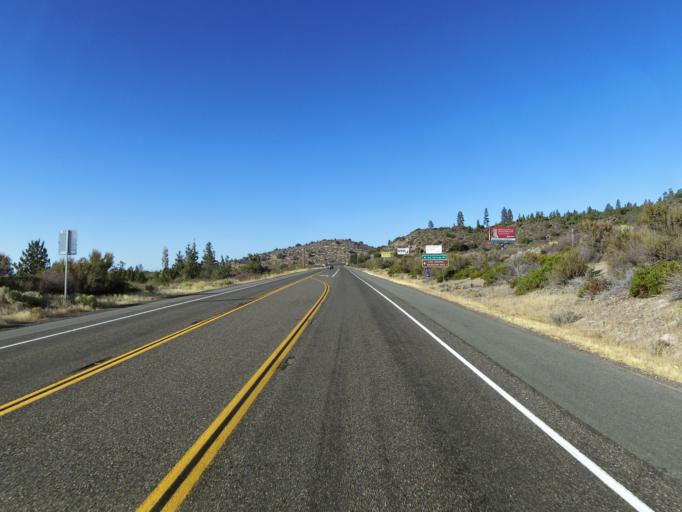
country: US
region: California
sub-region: Siskiyou County
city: Weed
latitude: 41.4709
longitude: -122.3523
